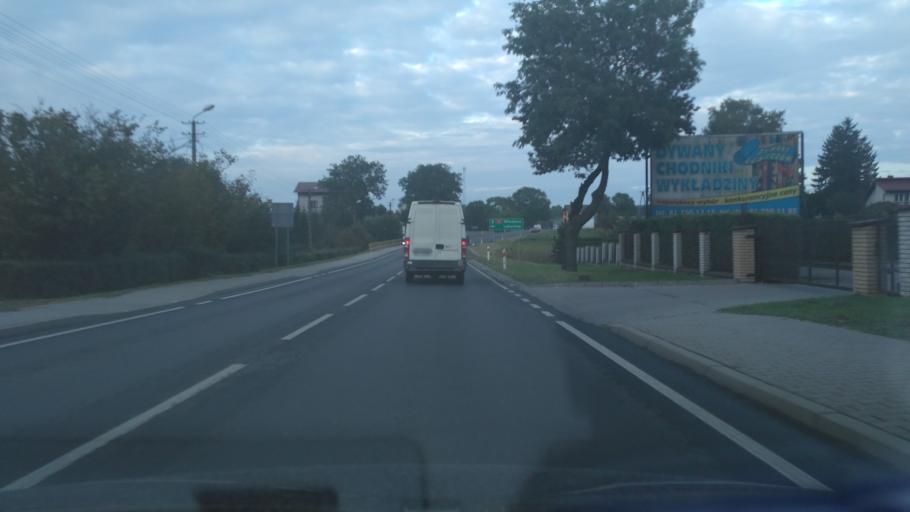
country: PL
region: Lublin Voivodeship
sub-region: Powiat leczynski
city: Spiczyn
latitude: 51.3033
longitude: 22.7294
